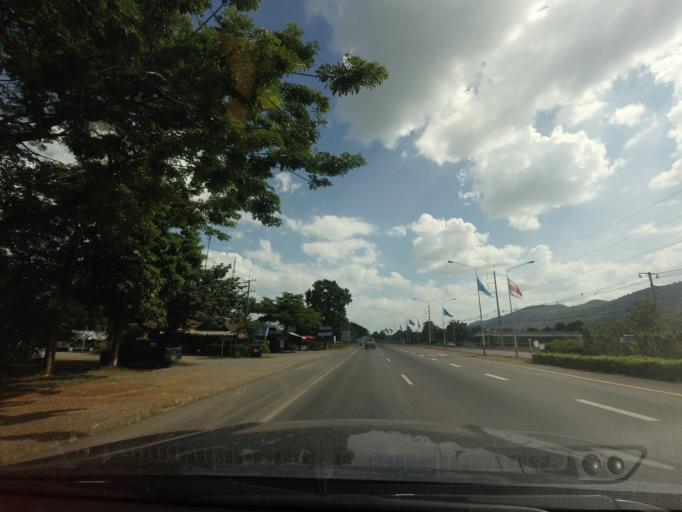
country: TH
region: Phetchabun
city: Wichian Buri
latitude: 15.6543
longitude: 101.0399
